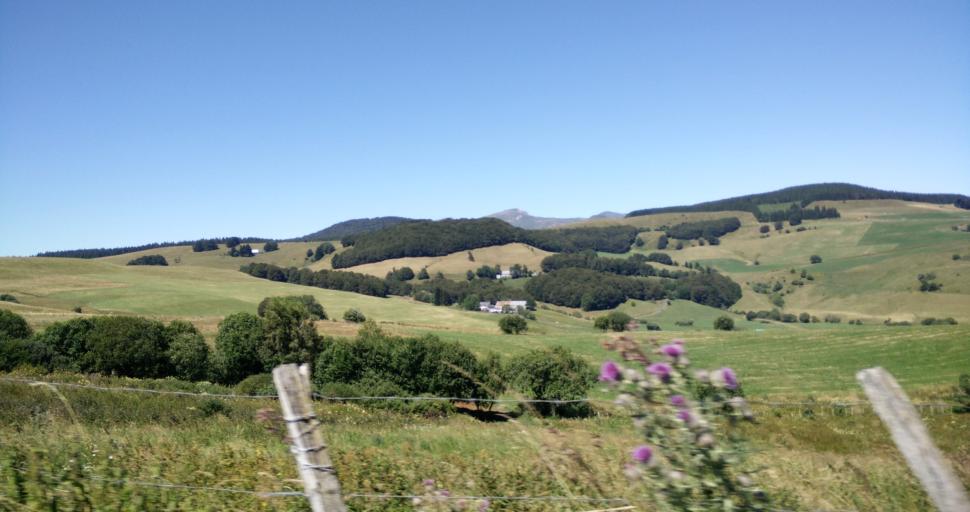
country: FR
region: Auvergne
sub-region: Departement du Puy-de-Dome
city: Mont-Dore
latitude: 45.4744
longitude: 2.9259
